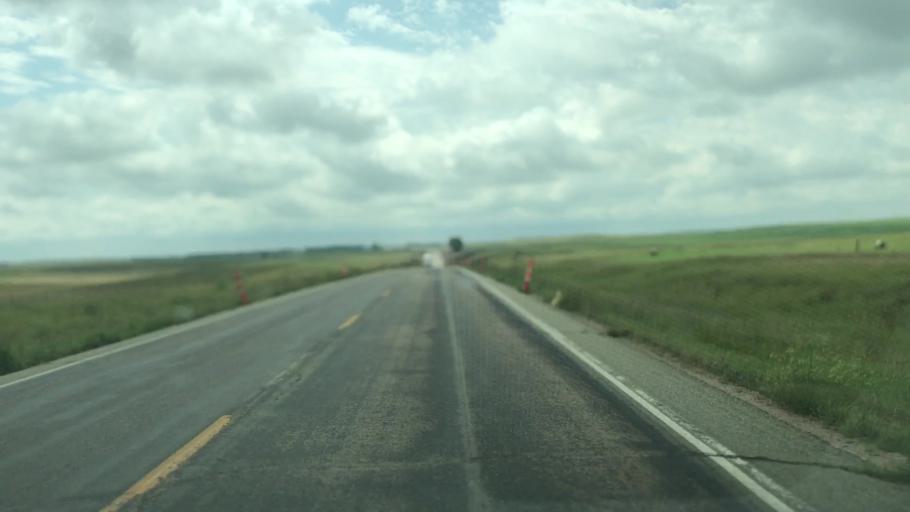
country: US
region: Nebraska
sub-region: Cherry County
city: Valentine
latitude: 43.0576
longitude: -100.5949
